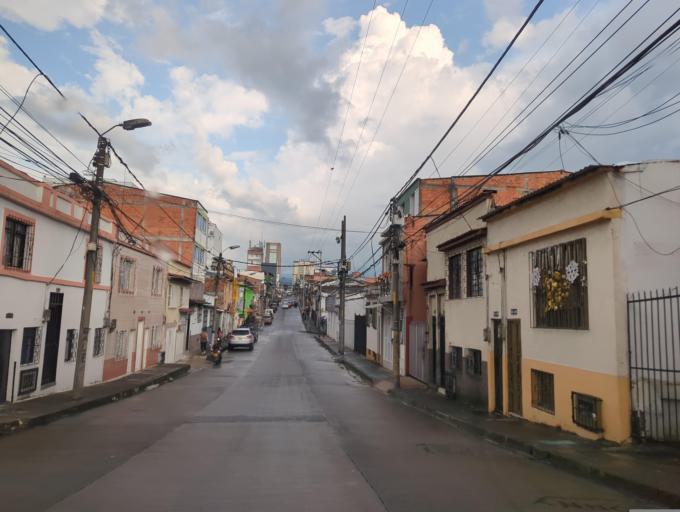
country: CO
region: Risaralda
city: Pereira
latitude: 4.8131
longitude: -75.7019
